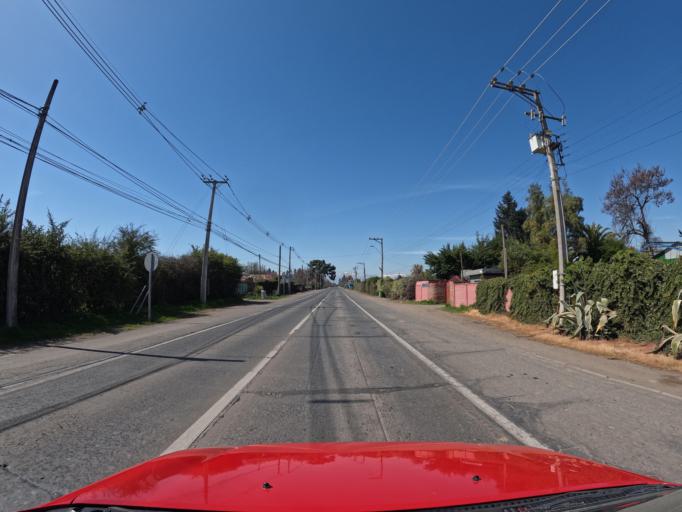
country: CL
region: Maule
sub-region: Provincia de Curico
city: Curico
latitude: -34.9642
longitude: -71.1856
